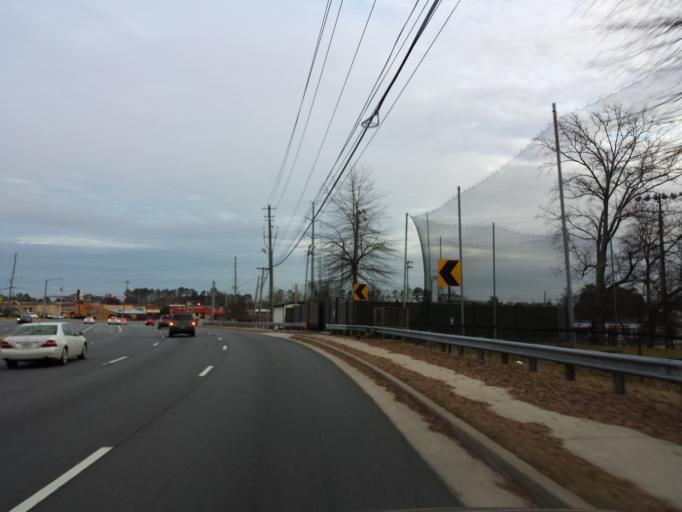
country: US
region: Georgia
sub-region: Fulton County
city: Sandy Springs
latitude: 33.9676
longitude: -84.4134
